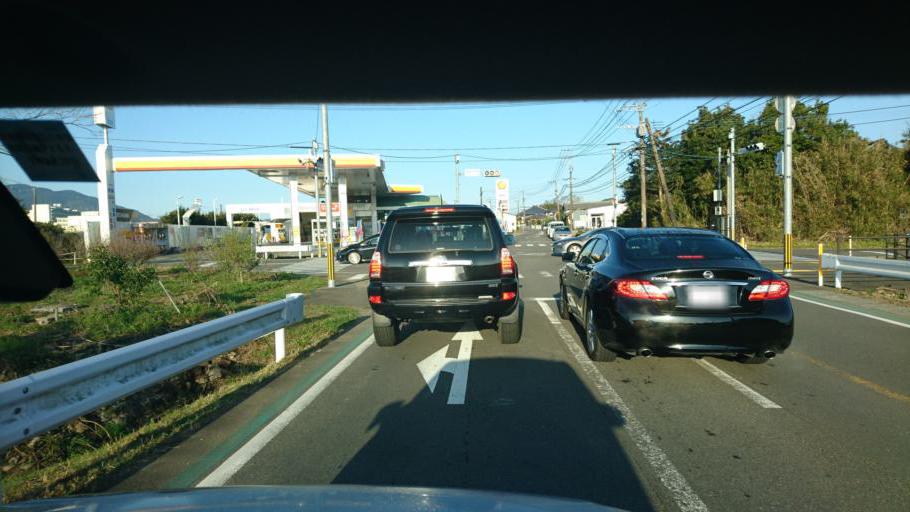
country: JP
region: Miyazaki
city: Miyazaki-shi
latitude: 31.8430
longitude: 131.4074
